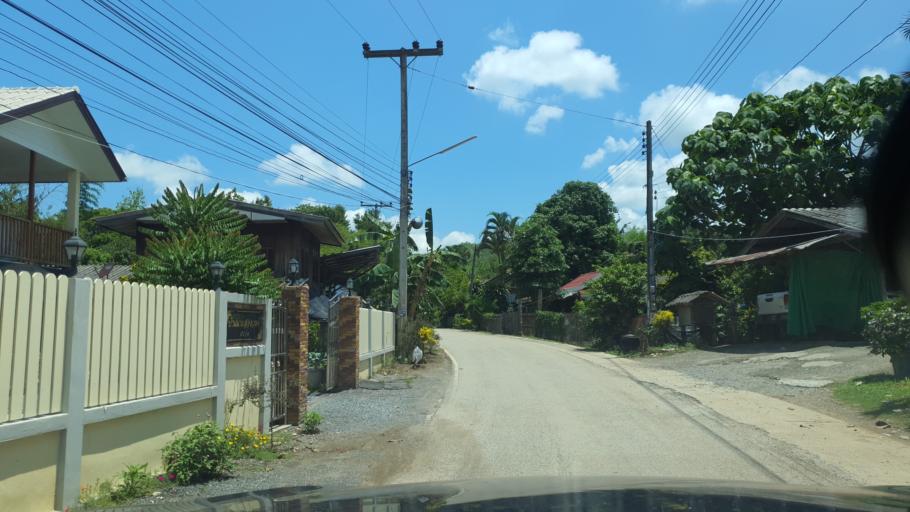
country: TH
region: Chiang Mai
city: Mae On
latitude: 18.8148
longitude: 99.2595
